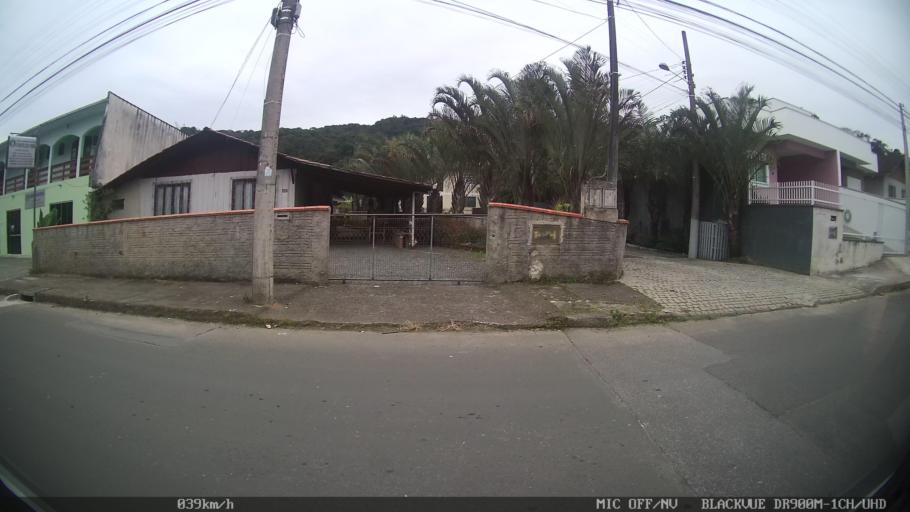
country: BR
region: Santa Catarina
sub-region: Joinville
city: Joinville
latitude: -26.2639
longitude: -48.8242
